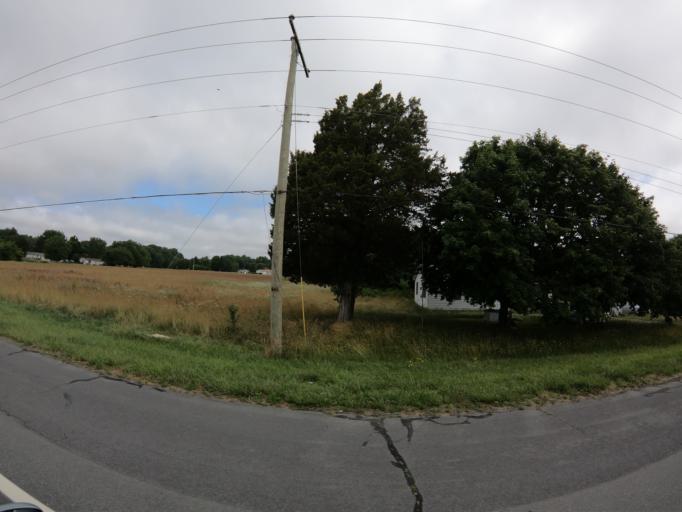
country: US
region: Delaware
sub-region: Kent County
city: Riverview
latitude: 39.0117
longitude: -75.5121
